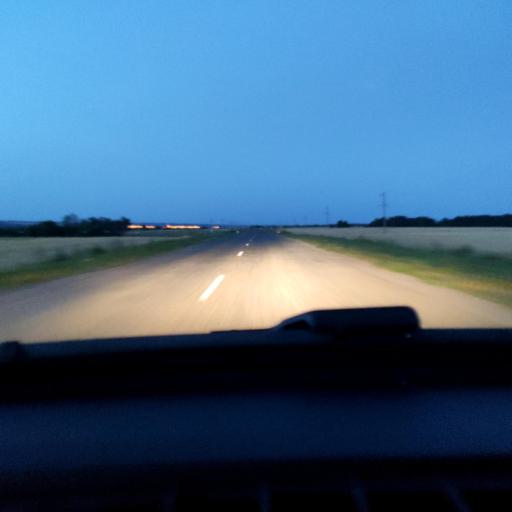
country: RU
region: Lipetsk
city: Zadonsk
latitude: 52.3103
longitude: 38.8933
